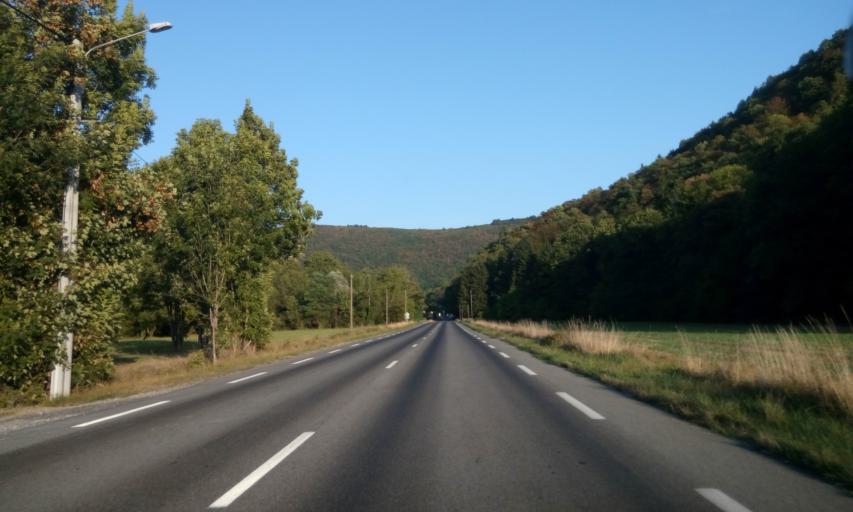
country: FR
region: Rhone-Alpes
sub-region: Departement de l'Ain
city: Poncin
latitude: 46.0764
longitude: 5.4346
